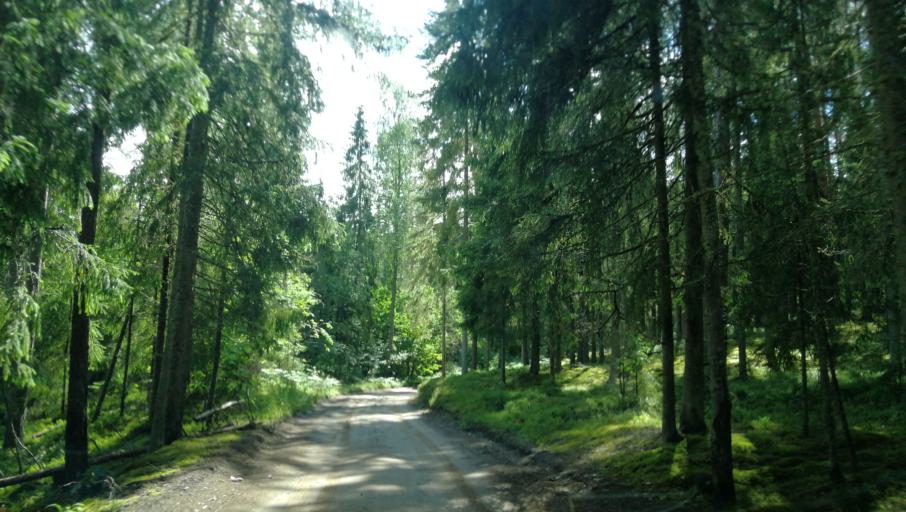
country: LV
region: Cesu Rajons
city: Cesis
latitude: 57.3046
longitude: 25.2115
